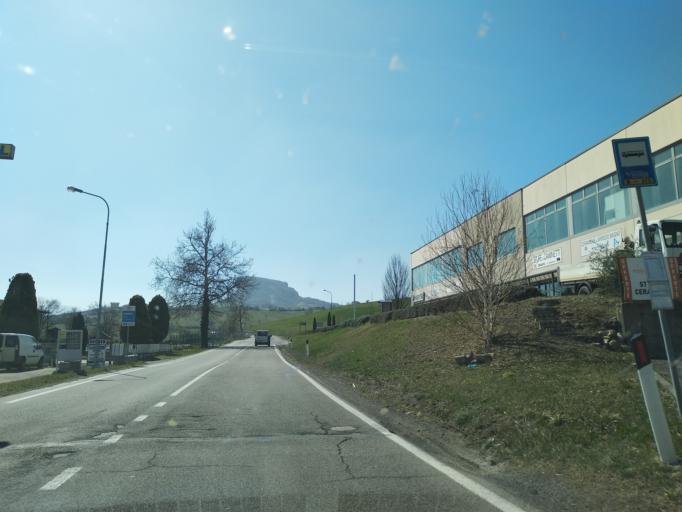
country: IT
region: Emilia-Romagna
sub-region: Provincia di Reggio Emilia
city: Felina
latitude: 44.4443
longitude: 10.4455
